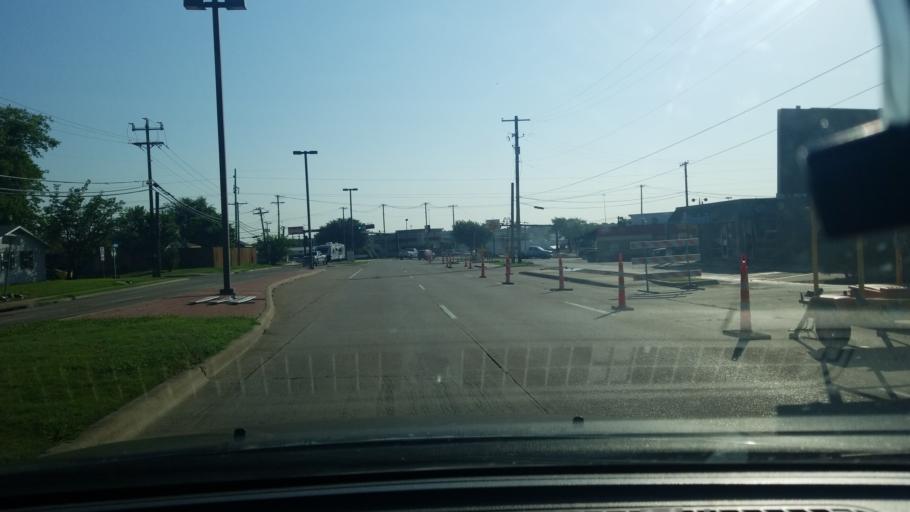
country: US
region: Texas
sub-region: Dallas County
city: Mesquite
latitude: 32.8104
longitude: -96.6357
